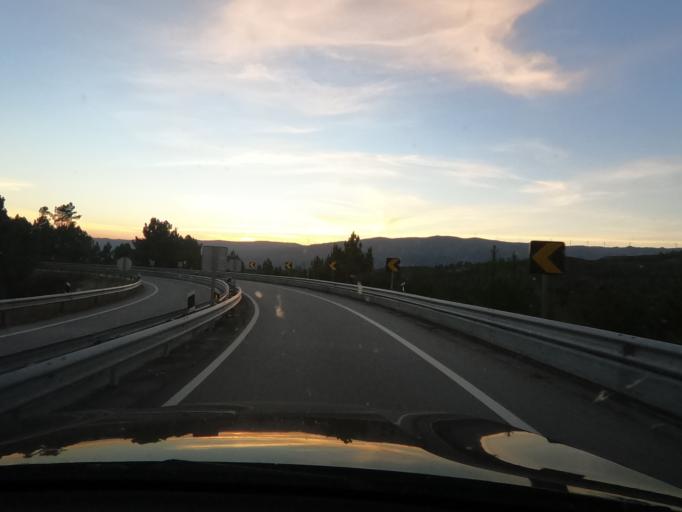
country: PT
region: Vila Real
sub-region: Vila Real
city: Vila Real
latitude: 41.3302
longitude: -7.6737
